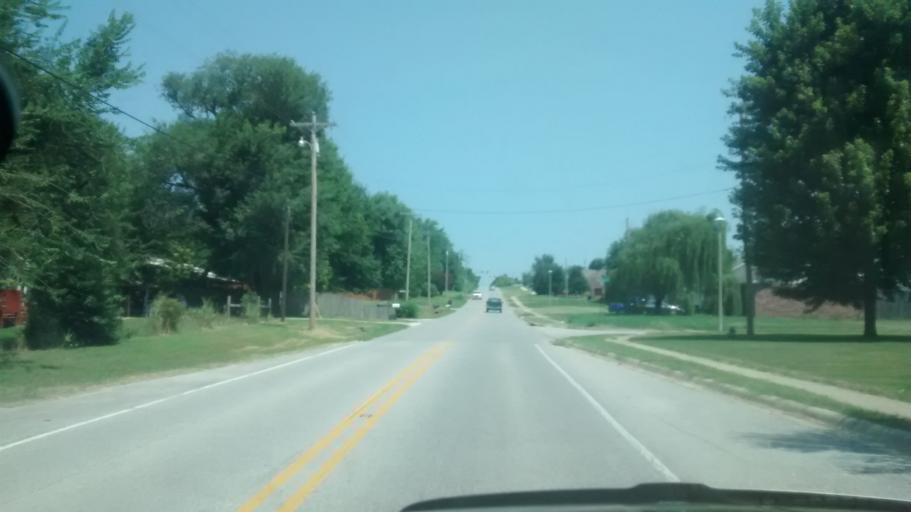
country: US
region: Arkansas
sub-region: Washington County
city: Farmington
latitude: 36.0755
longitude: -94.2533
